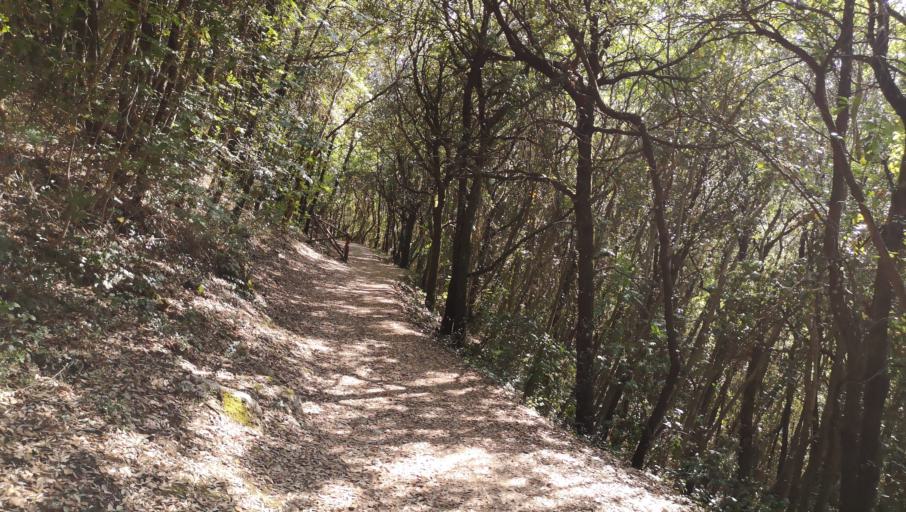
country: IT
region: Umbria
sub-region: Provincia di Terni
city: Narni
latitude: 42.5089
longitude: 12.5361
